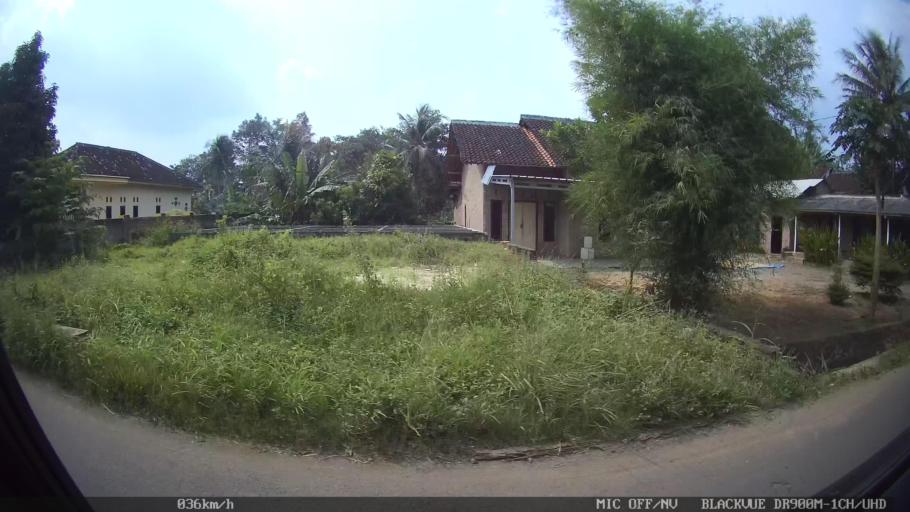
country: ID
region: Lampung
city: Gadingrejo
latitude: -5.3495
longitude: 105.0274
